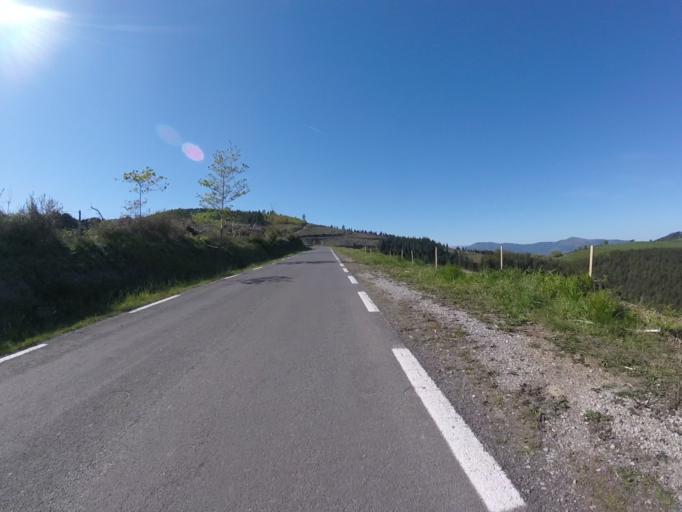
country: ES
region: Basque Country
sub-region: Provincia de Guipuzcoa
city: Errezil
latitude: 43.2044
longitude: -2.1981
